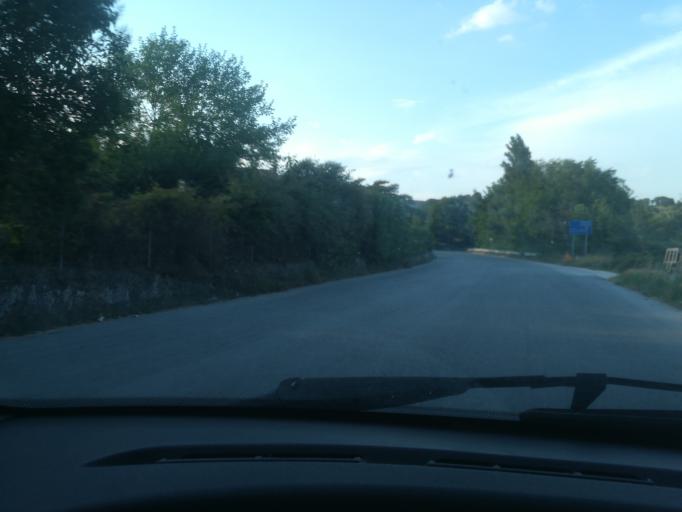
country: IT
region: The Marches
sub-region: Provincia di Macerata
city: Caldarola
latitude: 43.1514
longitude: 13.2196
